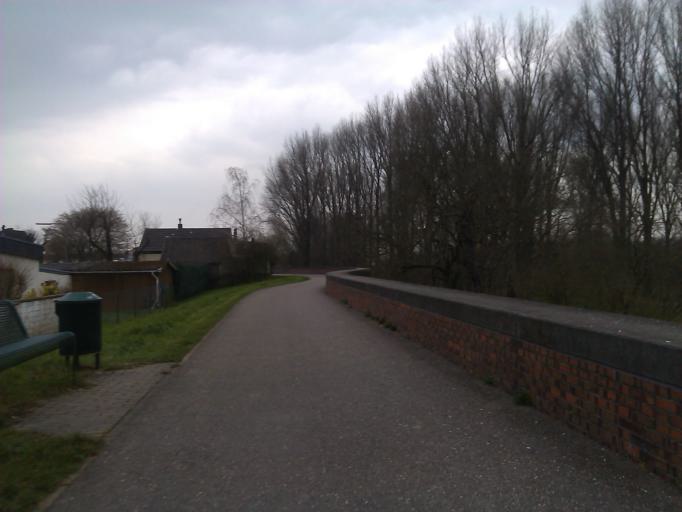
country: DE
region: North Rhine-Westphalia
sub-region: Regierungsbezirk Koln
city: Leverkusen
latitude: 51.0427
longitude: 6.9331
